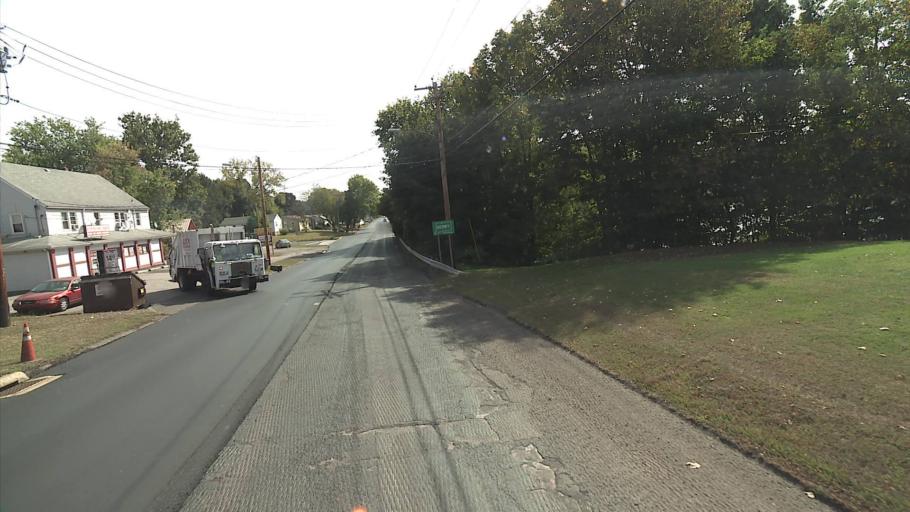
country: US
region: Connecticut
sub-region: Fairfield County
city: Shelton
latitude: 41.3301
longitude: -73.1083
